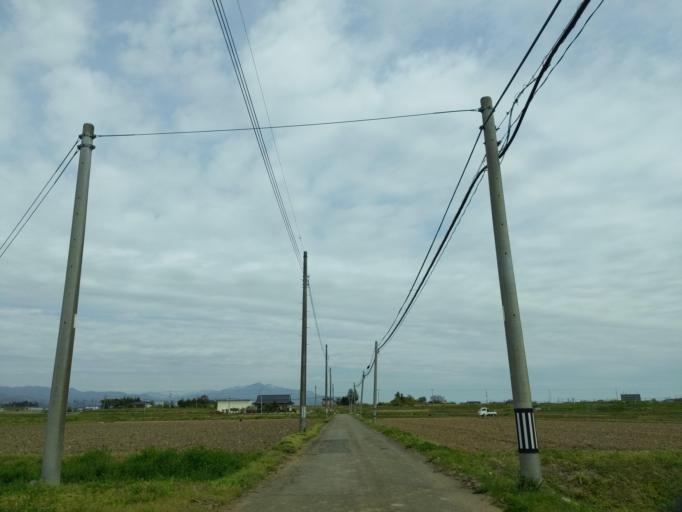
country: JP
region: Fukushima
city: Koriyama
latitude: 37.3777
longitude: 140.3237
